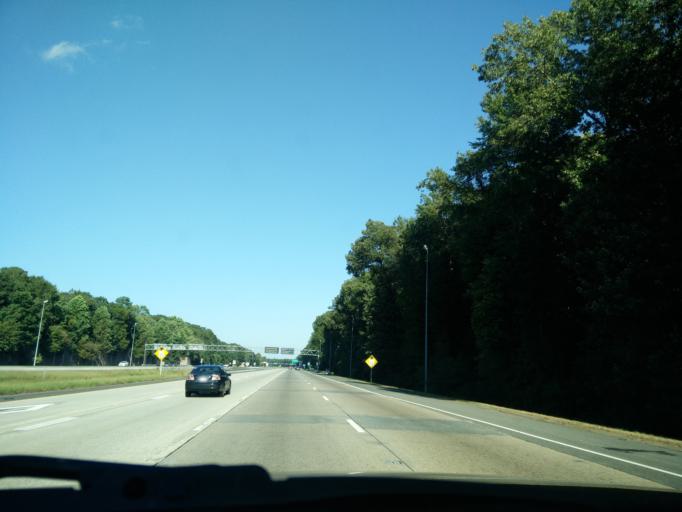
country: US
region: Virginia
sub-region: City of Chesapeake
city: Chesapeake
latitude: 36.7924
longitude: -76.2164
